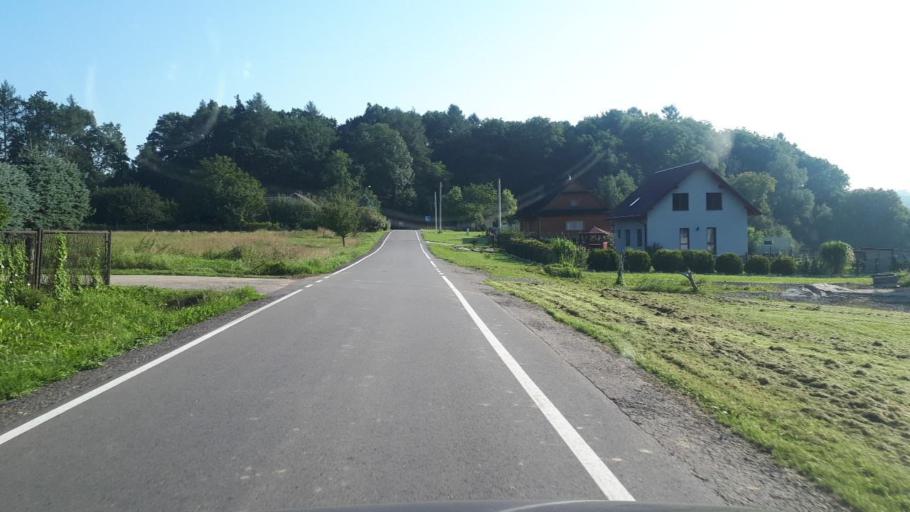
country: PL
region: Silesian Voivodeship
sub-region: Powiat cieszynski
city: Piersciec
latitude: 49.8487
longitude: 18.8346
